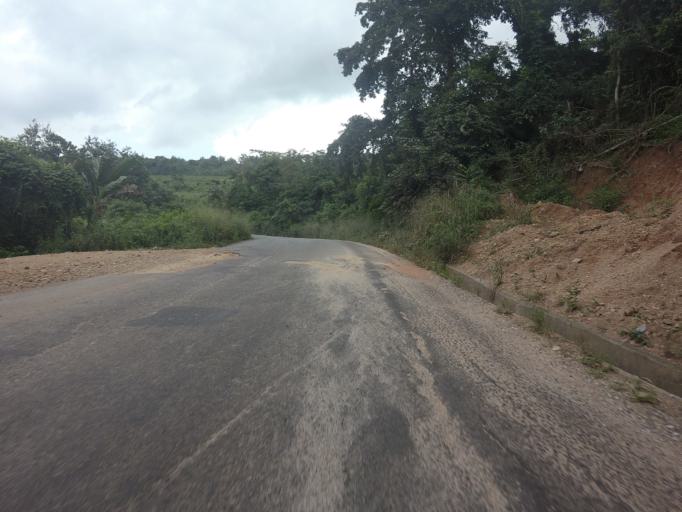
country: GH
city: Akropong
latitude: 5.9600
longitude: -0.1176
